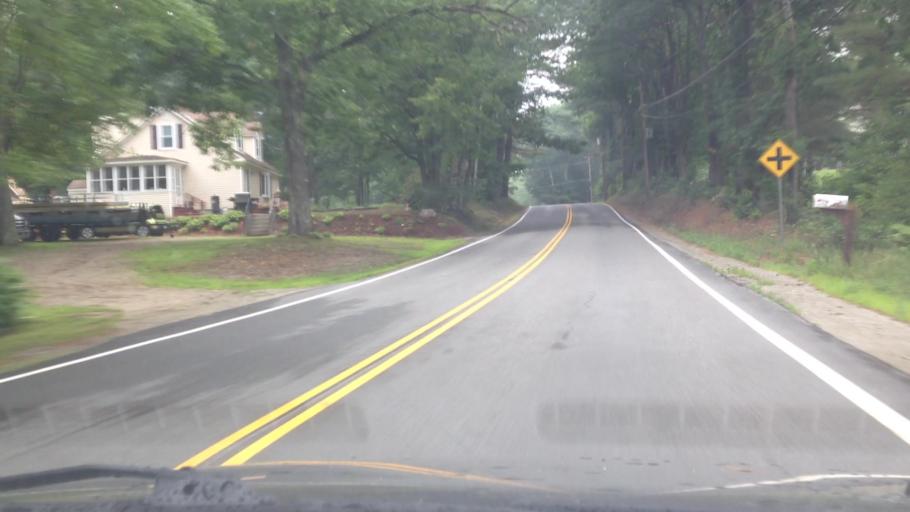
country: US
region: New Hampshire
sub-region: Cheshire County
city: Marlborough
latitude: 42.8812
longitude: -72.1938
